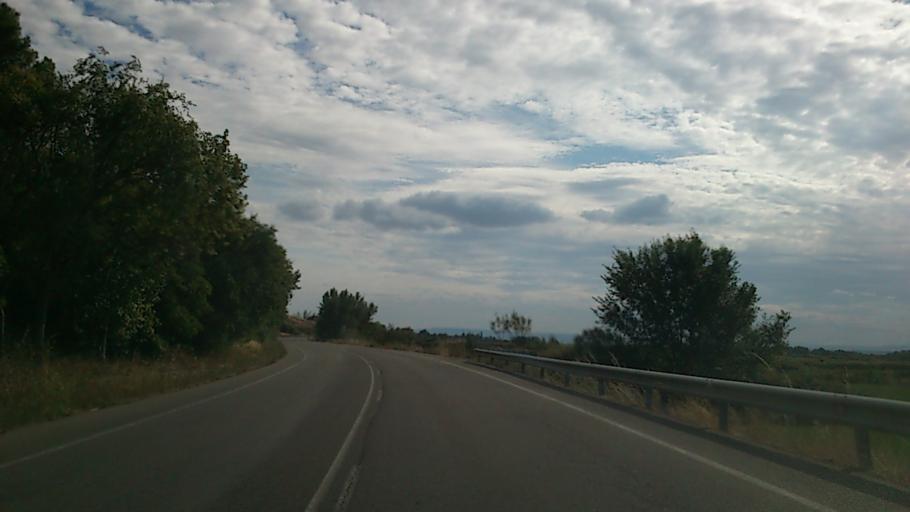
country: ES
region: Aragon
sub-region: Provincia de Zaragoza
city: Villanueva de Gallego
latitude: 41.7842
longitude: -0.7873
